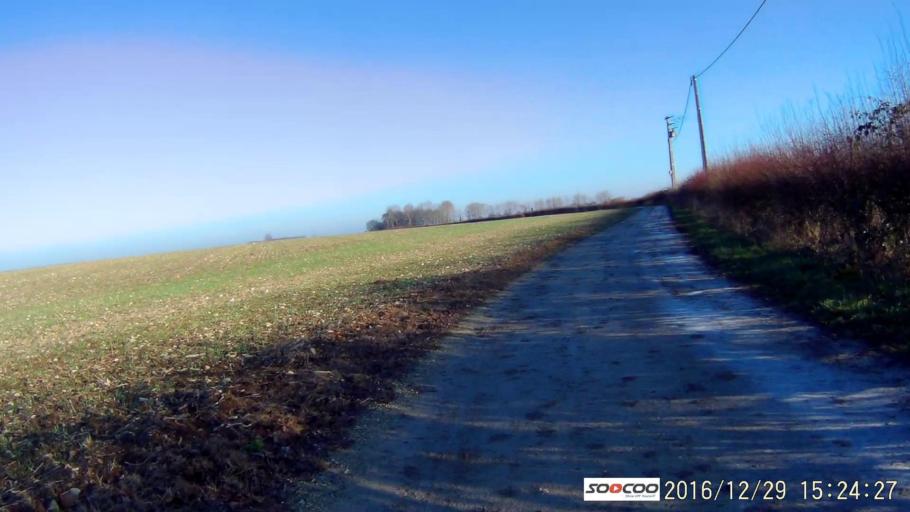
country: FR
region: Centre
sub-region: Departement de l'Indre
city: Neuvy-Pailloux
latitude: 46.9370
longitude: 1.8198
